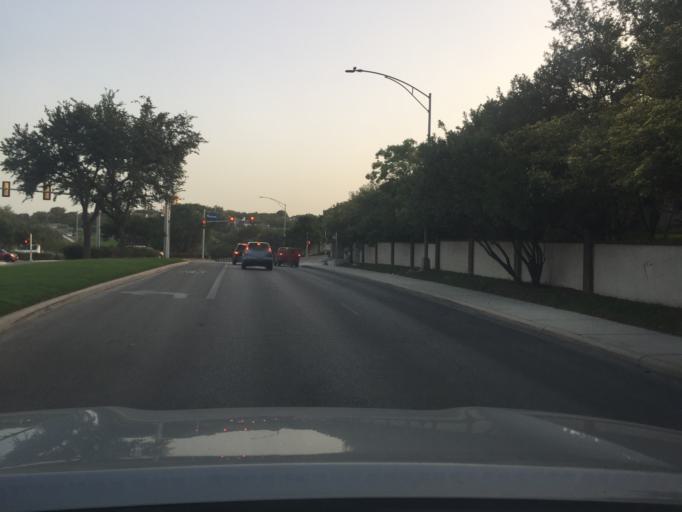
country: US
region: Texas
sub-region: Bexar County
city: Hollywood Park
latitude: 29.6396
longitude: -98.4943
